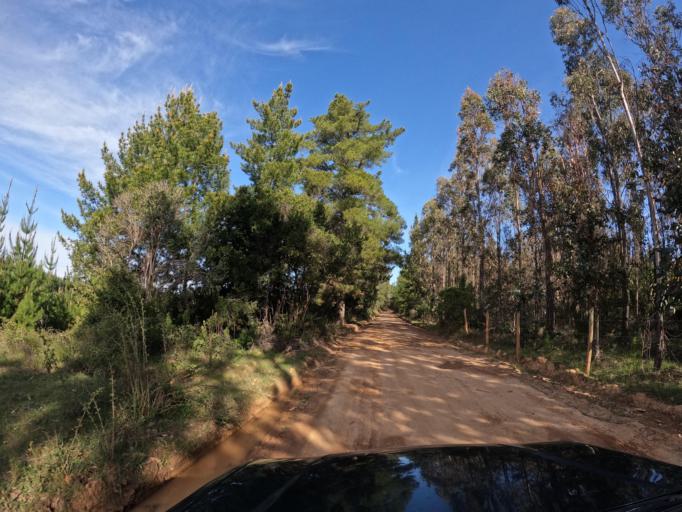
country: CL
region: Biobio
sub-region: Provincia de Biobio
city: La Laja
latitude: -37.1205
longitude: -72.7374
